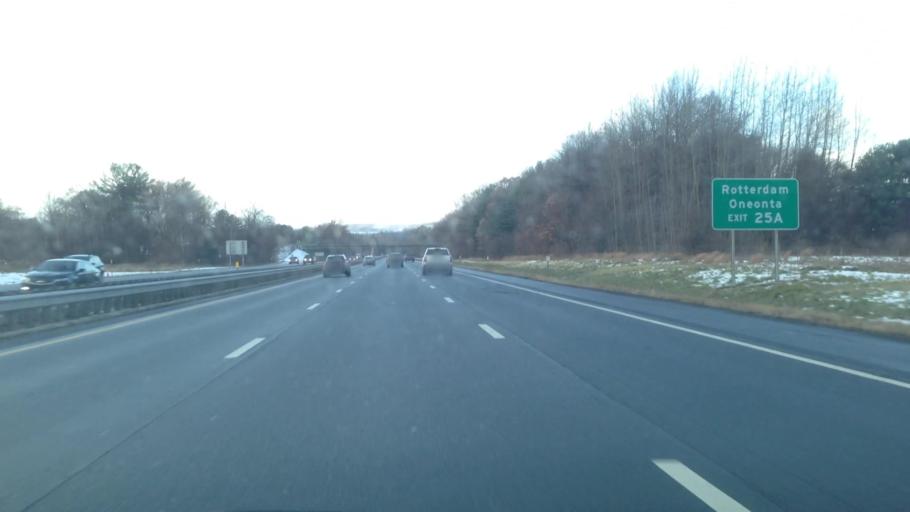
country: US
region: New York
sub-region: Schenectady County
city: Rotterdam
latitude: 42.7780
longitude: -73.9991
